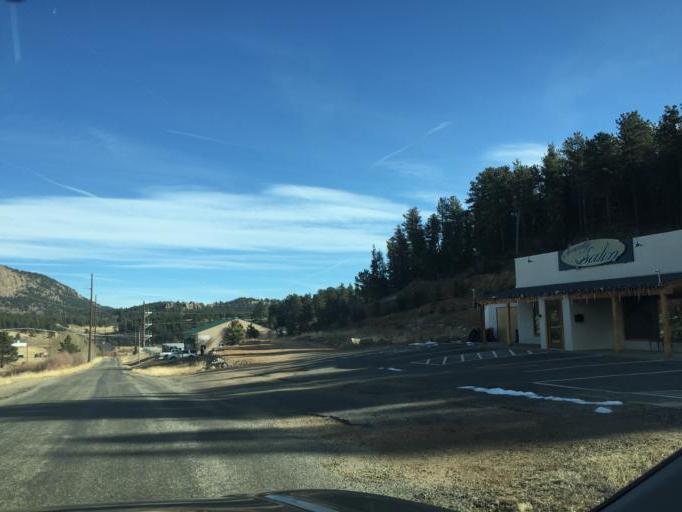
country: US
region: Colorado
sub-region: Jefferson County
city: Evergreen
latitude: 39.4382
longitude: -105.4537
